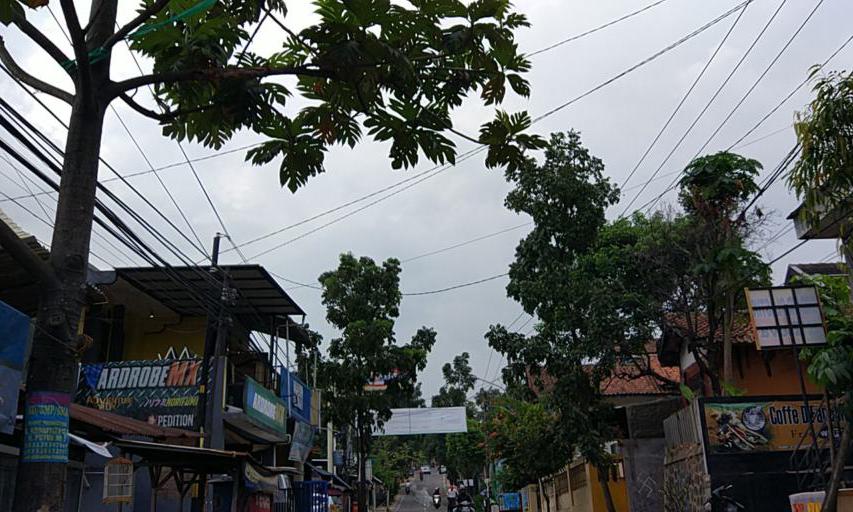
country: ID
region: West Java
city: Bandung
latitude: -6.9021
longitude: 107.6804
